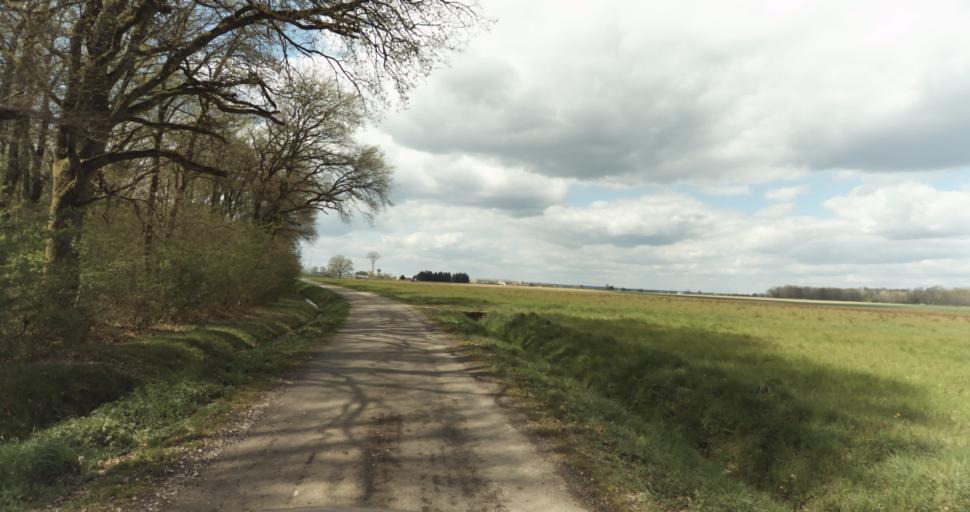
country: FR
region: Bourgogne
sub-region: Departement de la Cote-d'Or
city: Auxonne
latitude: 47.1749
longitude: 5.4139
